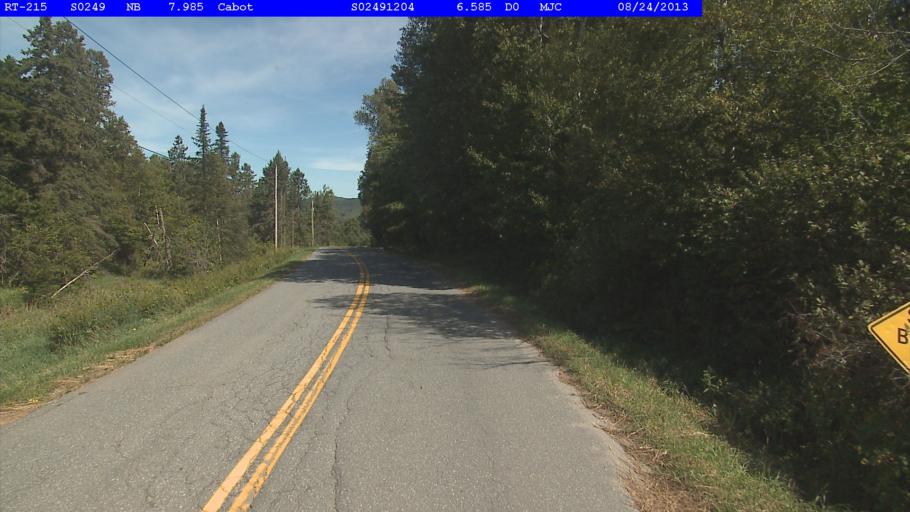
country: US
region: Vermont
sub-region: Caledonia County
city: Hardwick
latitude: 44.4403
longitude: -72.2718
